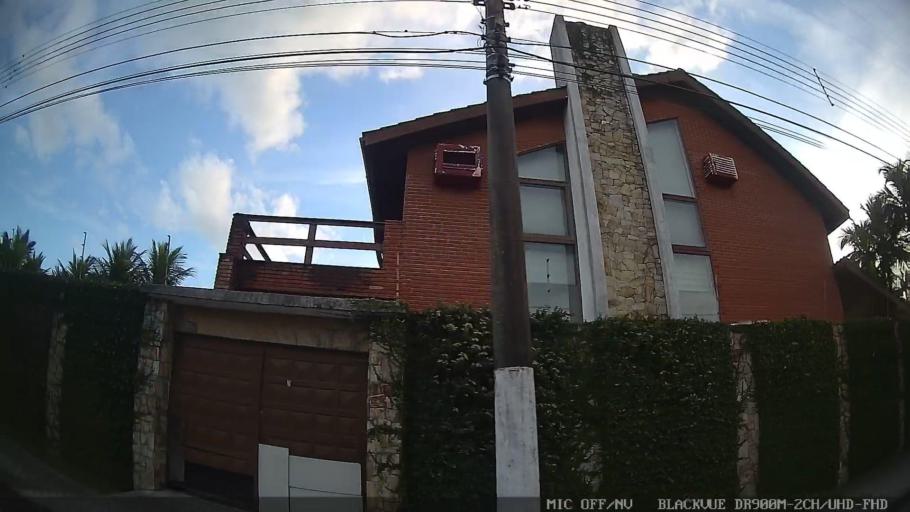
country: BR
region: Sao Paulo
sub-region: Guaruja
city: Guaruja
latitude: -23.9853
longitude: -46.2267
